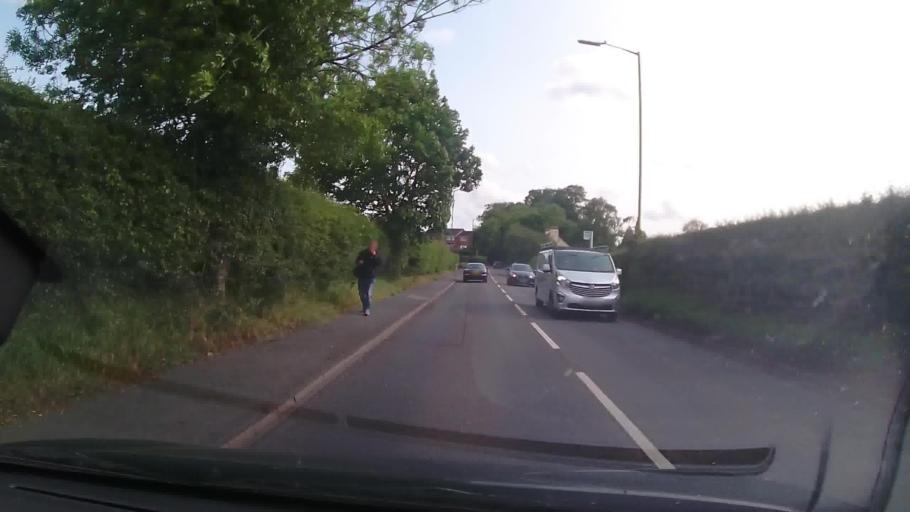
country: GB
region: England
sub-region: Shropshire
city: Shrewsbury
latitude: 52.7363
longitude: -2.7460
